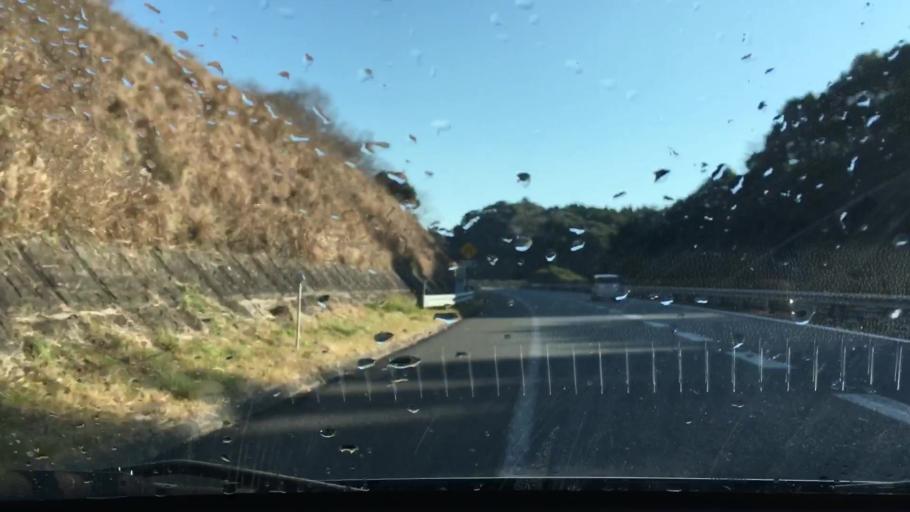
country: JP
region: Kagoshima
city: Kokubu-matsuki
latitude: 31.7436
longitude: 130.8036
